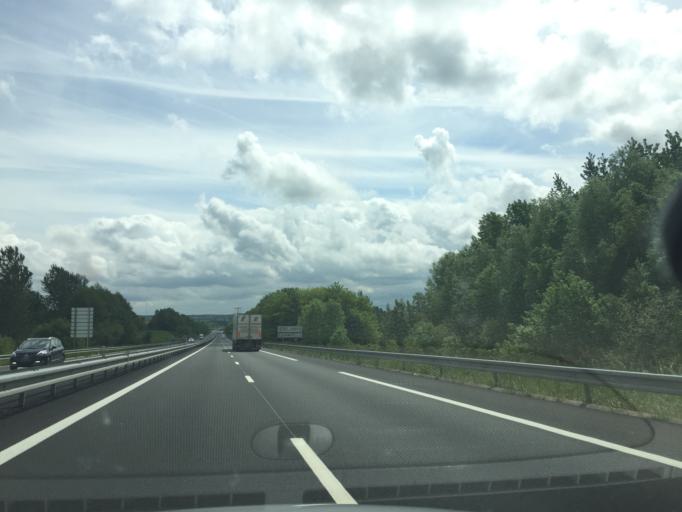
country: FR
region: Pays de la Loire
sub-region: Departement de la Sarthe
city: Ecommoy
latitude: 47.8350
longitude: 0.3058
